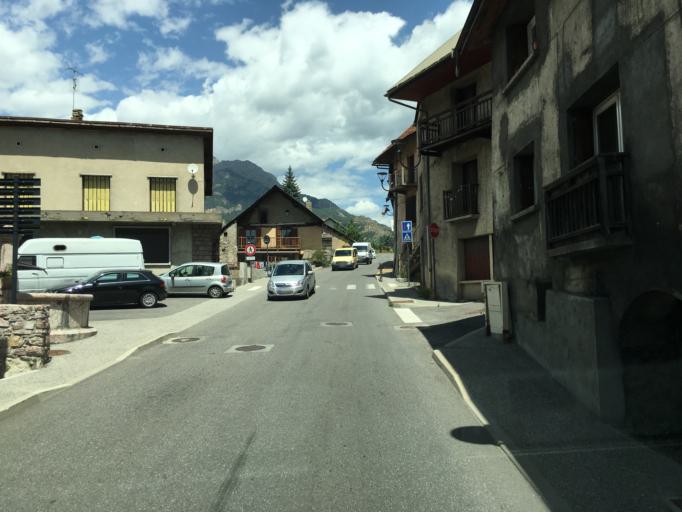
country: FR
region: Provence-Alpes-Cote d'Azur
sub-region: Departement des Hautes-Alpes
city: Saint-Martin-de-Queyrieres
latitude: 44.7947
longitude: 6.5626
